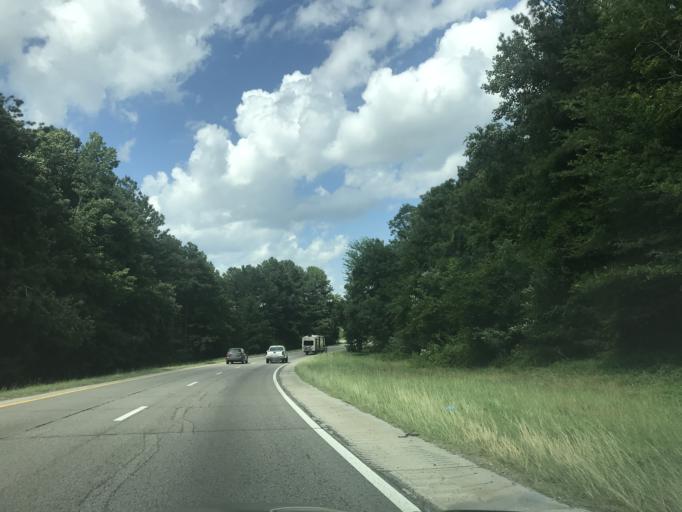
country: US
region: North Carolina
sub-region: Wake County
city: Garner
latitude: 35.7517
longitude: -78.5936
